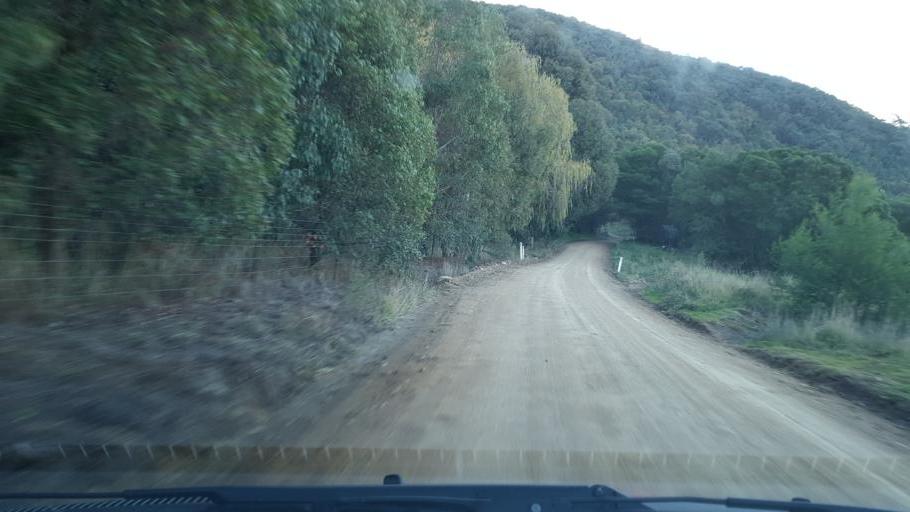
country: AU
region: New South Wales
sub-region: Palerang
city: Bungendore
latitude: -35.1838
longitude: 149.3985
